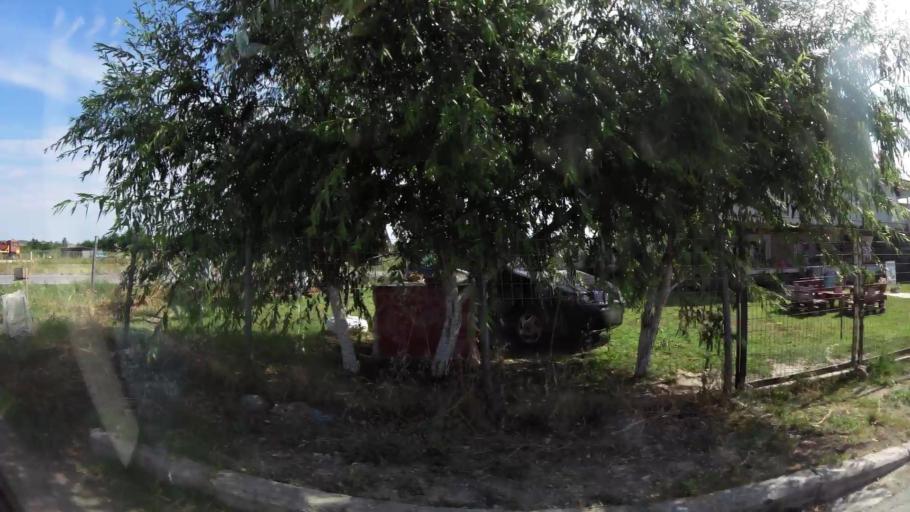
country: GR
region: Central Macedonia
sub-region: Nomos Pierias
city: Katerini
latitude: 40.2830
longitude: 22.4965
